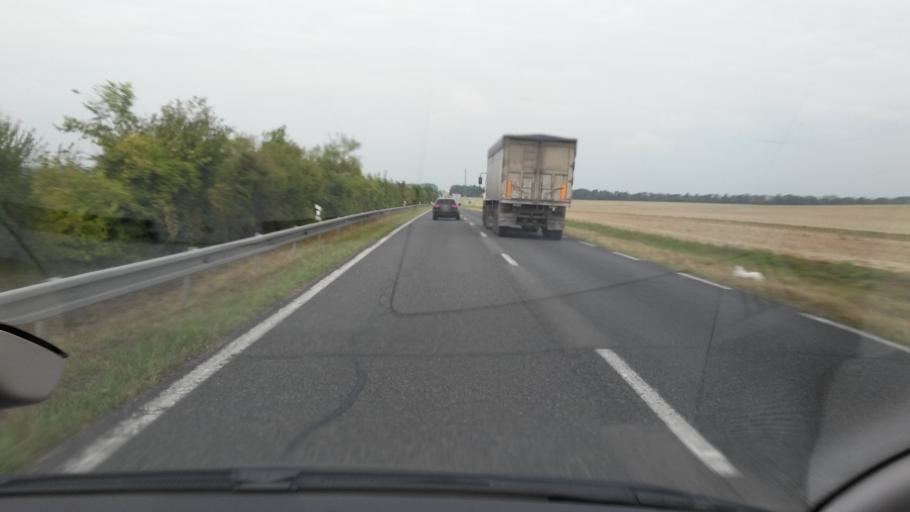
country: FR
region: Champagne-Ardenne
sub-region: Departement de la Marne
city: Warmeriville
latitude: 49.3744
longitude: 4.2192
